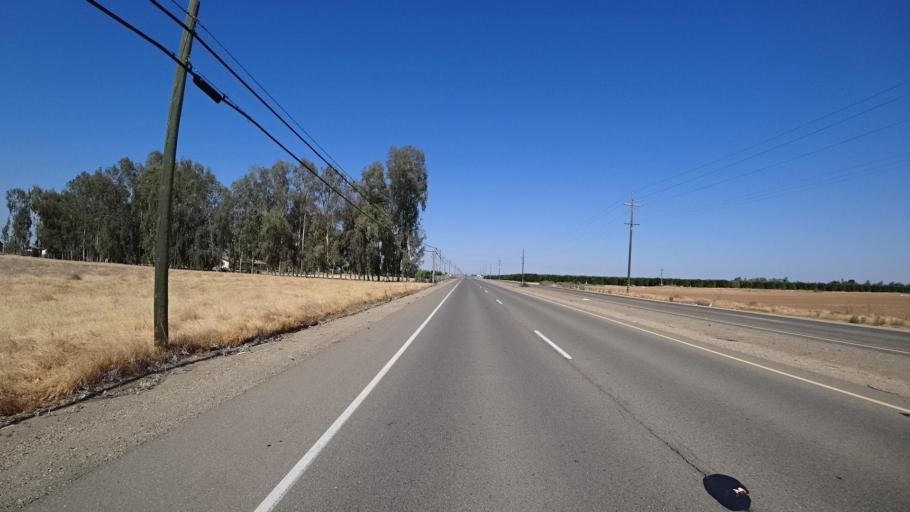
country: US
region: California
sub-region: Fresno County
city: Sunnyside
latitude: 36.7073
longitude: -119.6669
